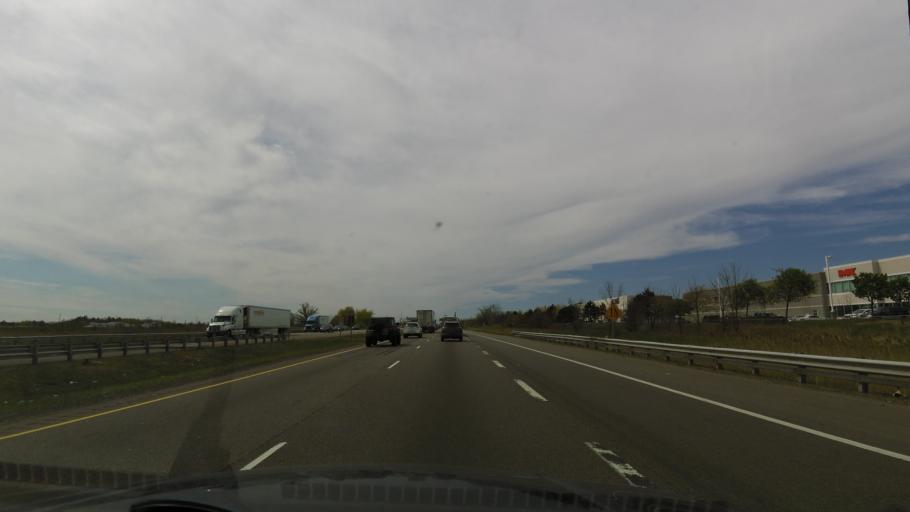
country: CA
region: Ontario
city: Oakville
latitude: 43.5153
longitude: -79.6990
